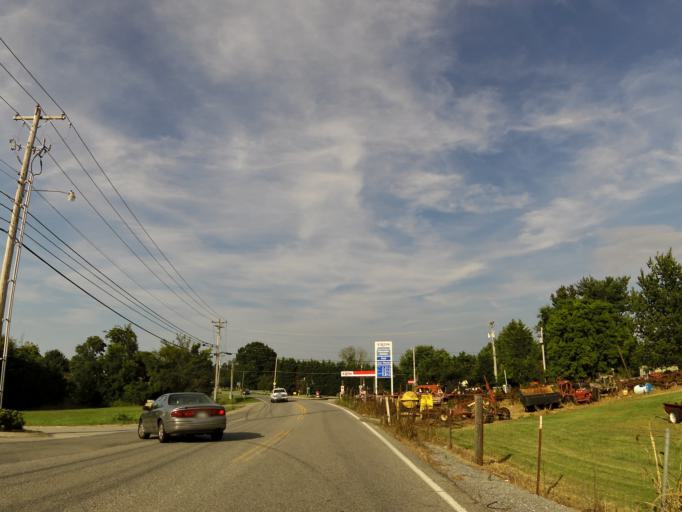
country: US
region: Tennessee
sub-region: Blount County
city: Eagleton Village
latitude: 35.7693
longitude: -83.9182
